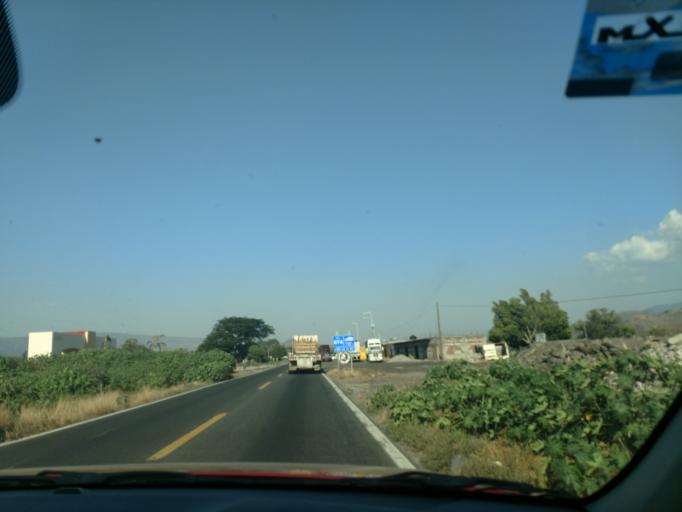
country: MX
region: Nayarit
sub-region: Ahuacatlan
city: Ahuacatlan
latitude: 21.0595
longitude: -104.5005
